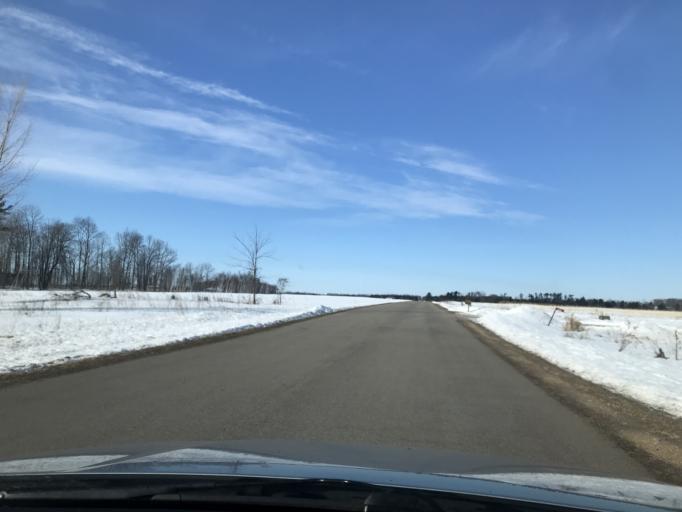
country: US
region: Wisconsin
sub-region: Oconto County
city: Oconto Falls
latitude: 44.9383
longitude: -88.1943
